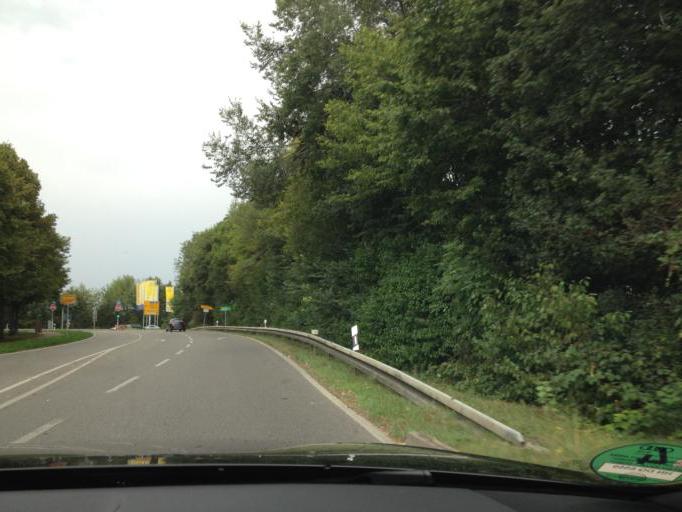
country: DE
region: Baden-Wuerttemberg
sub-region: Regierungsbezirk Stuttgart
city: Leinfelden-Echterdingen
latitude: 48.6909
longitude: 9.1751
